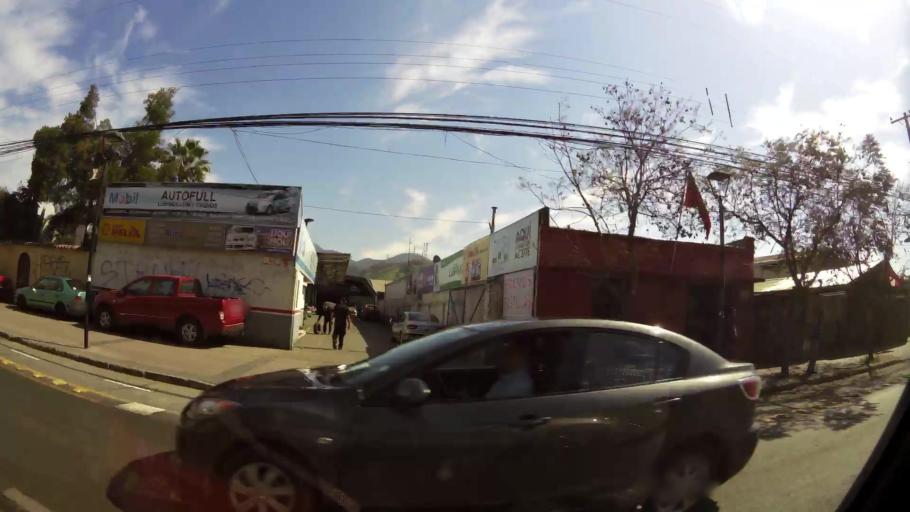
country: CL
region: Santiago Metropolitan
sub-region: Provincia de Talagante
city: Talagante
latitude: -33.6661
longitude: -70.9342
